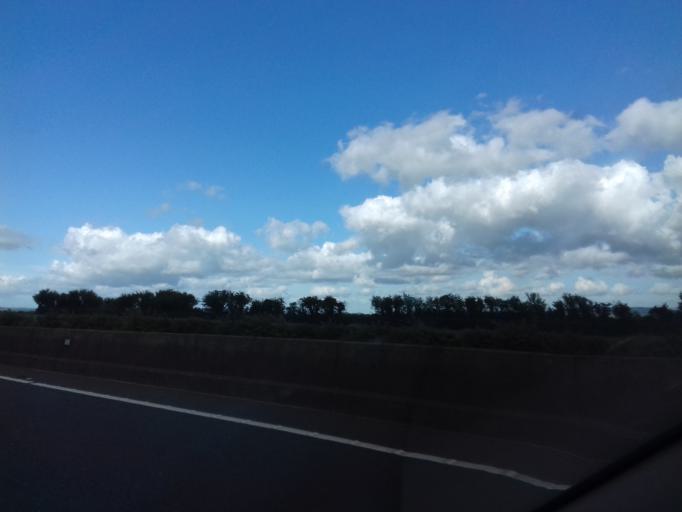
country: IE
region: Leinster
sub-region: Kilkenny
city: Kilkenny
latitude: 52.5519
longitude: -7.2483
